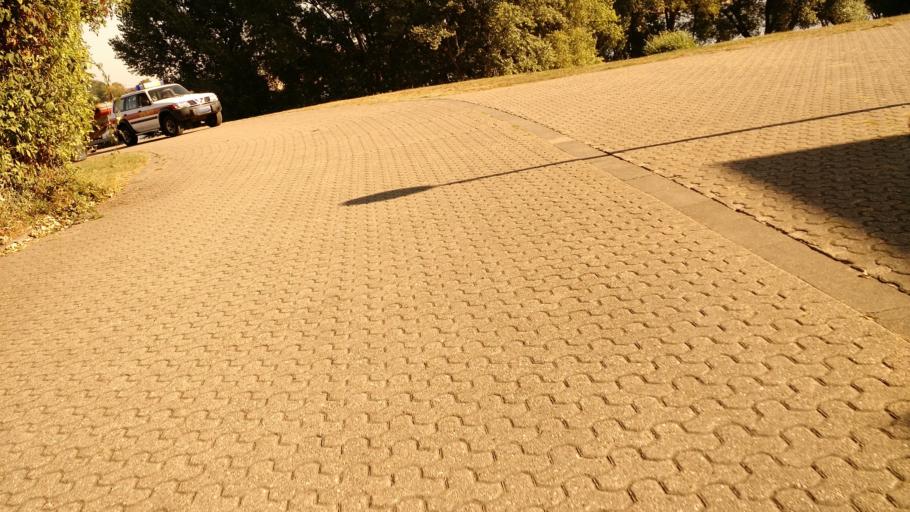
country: DE
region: North Rhine-Westphalia
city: Wesseling
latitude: 50.8236
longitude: 6.9884
